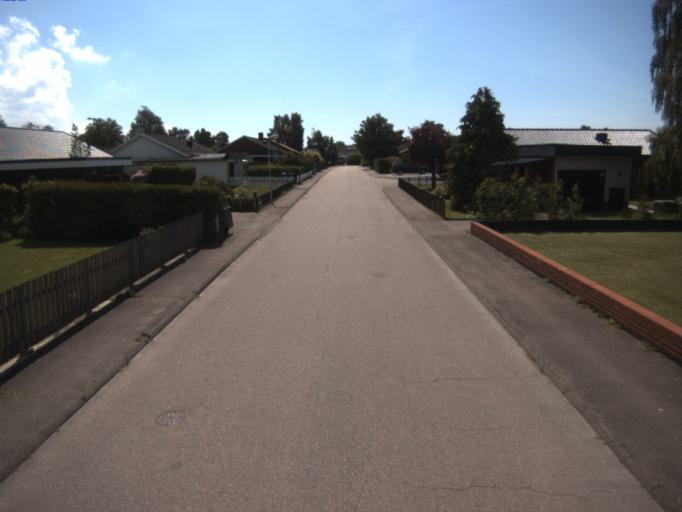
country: SE
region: Skane
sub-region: Helsingborg
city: Barslov
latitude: 56.0332
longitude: 12.8127
